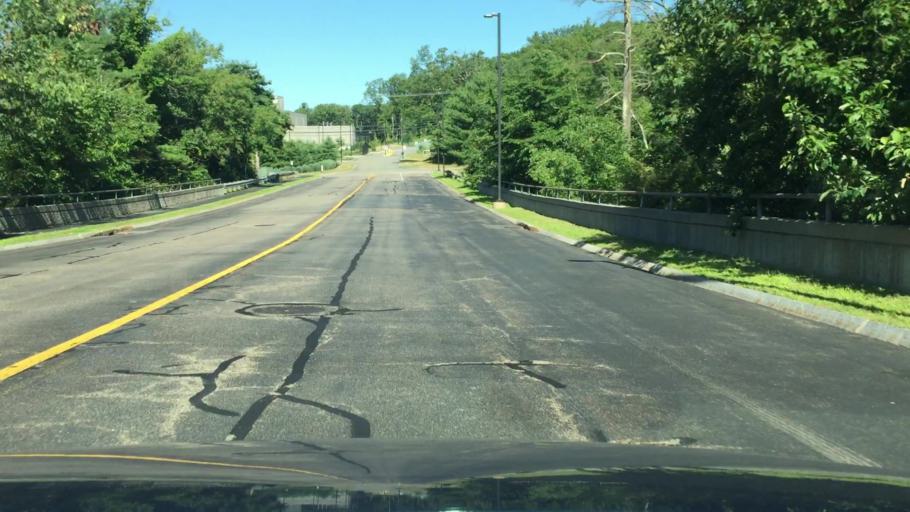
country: US
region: Massachusetts
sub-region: Middlesex County
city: Marlborough
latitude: 42.3262
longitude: -71.5884
